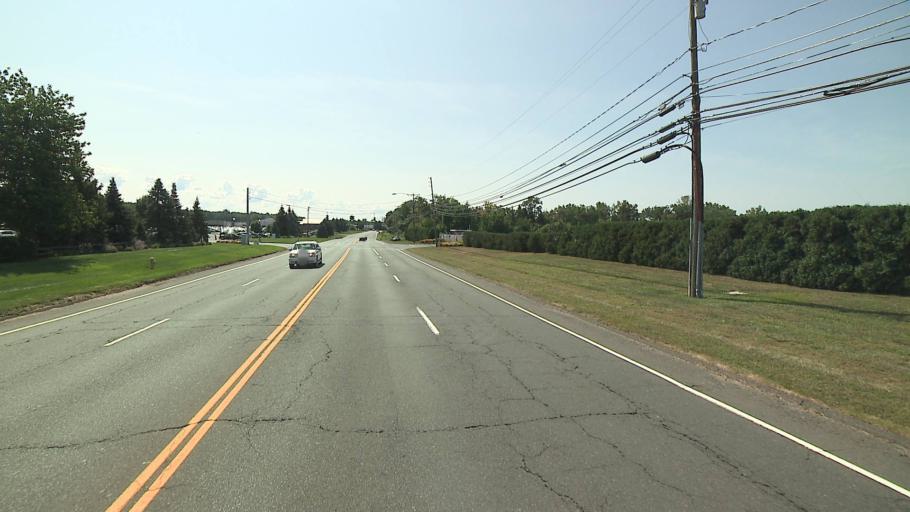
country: US
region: Connecticut
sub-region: Hartford County
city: Windsor Locks
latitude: 41.8888
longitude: -72.6081
